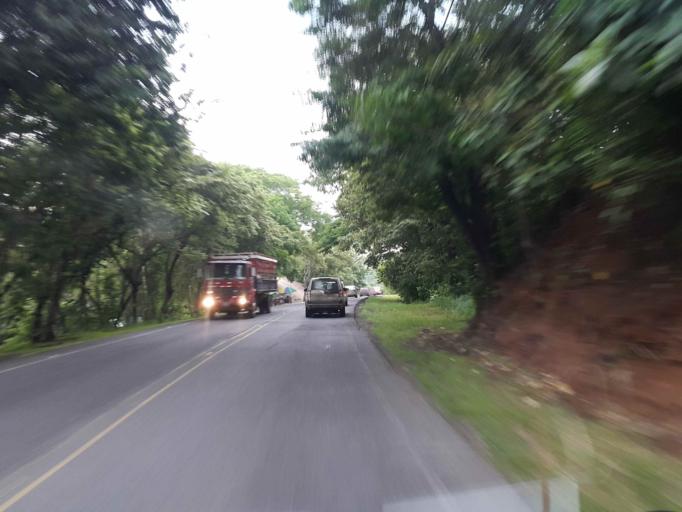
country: CR
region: Puntarenas
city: Miramar
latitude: 10.0750
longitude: -84.7769
